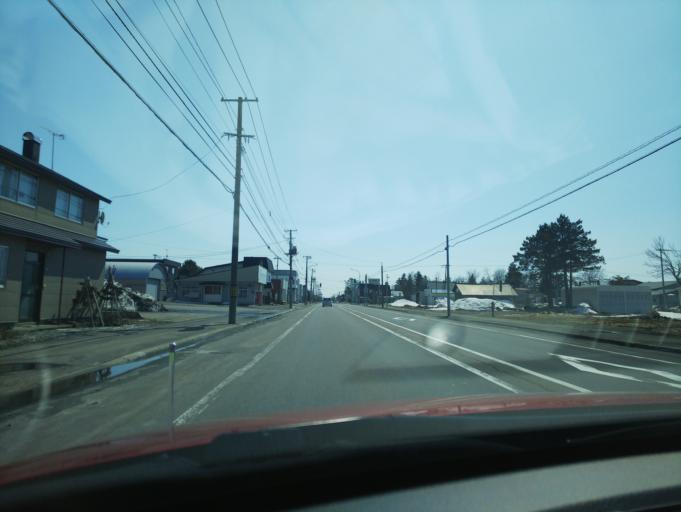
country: JP
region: Hokkaido
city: Nayoro
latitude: 44.2420
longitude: 142.3948
